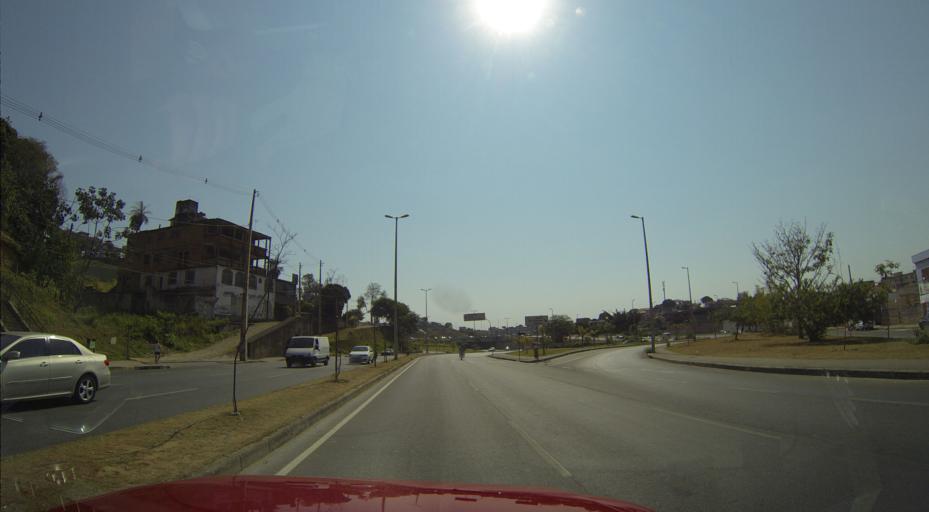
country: BR
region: Minas Gerais
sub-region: Belo Horizonte
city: Belo Horizonte
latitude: -19.8872
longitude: -43.9536
